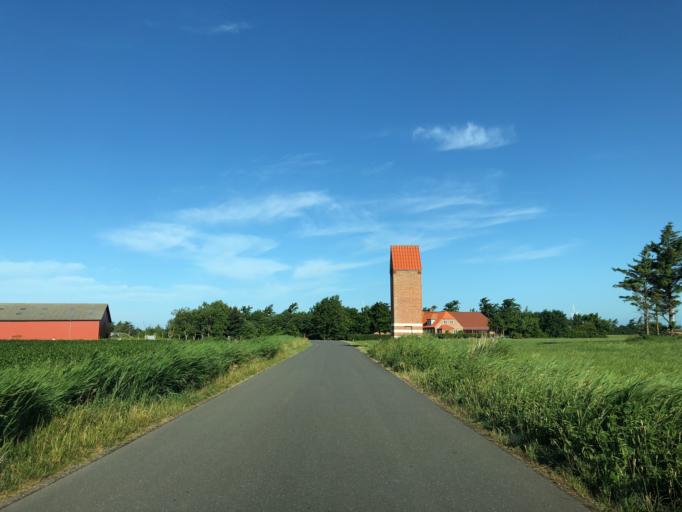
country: DK
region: Central Jutland
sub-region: Holstebro Kommune
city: Ulfborg
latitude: 56.3382
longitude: 8.2927
